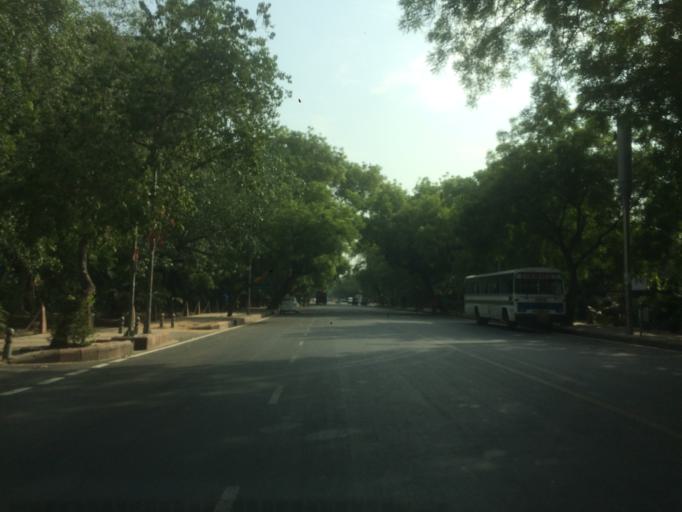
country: IN
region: NCT
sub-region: New Delhi
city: New Delhi
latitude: 28.6254
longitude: 77.2142
